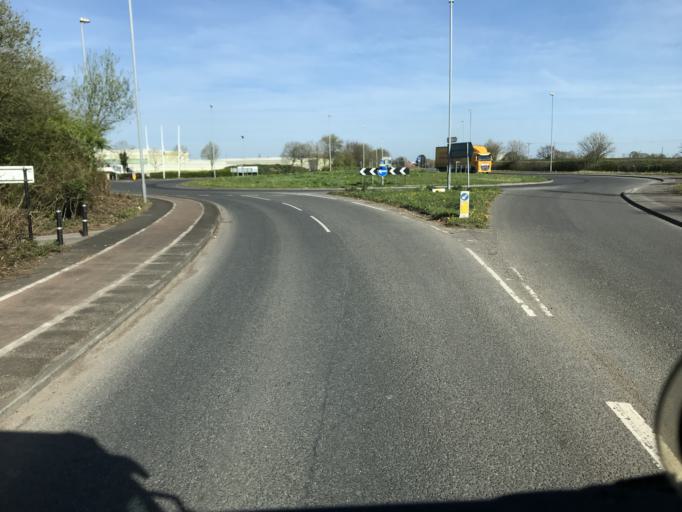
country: GB
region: England
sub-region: Cheshire West and Chester
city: Marston
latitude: 53.2458
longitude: -2.4708
